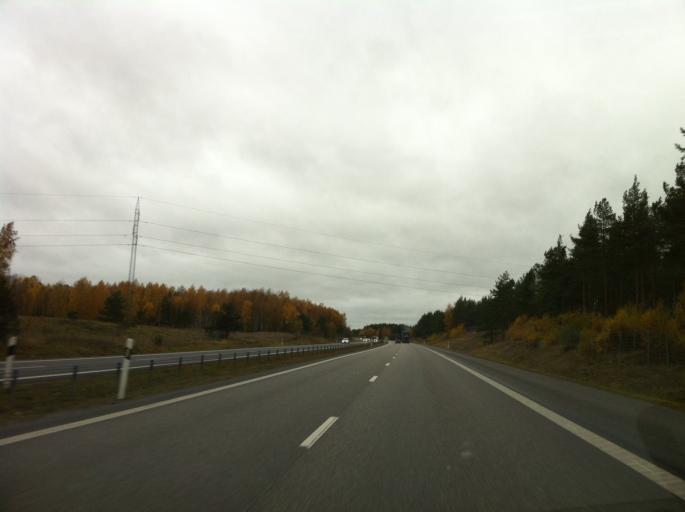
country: SE
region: OEstergoetland
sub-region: Linkopings Kommun
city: Vikingstad
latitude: 58.3858
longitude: 15.3786
